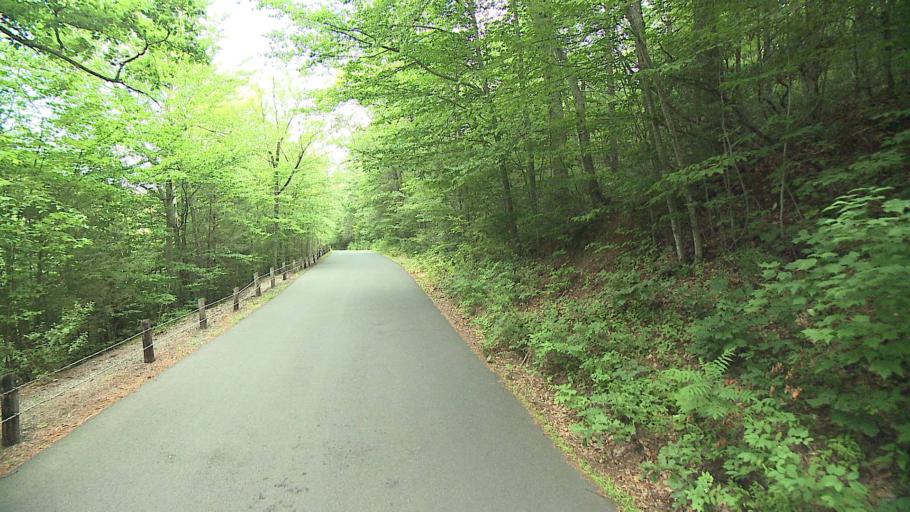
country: US
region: Connecticut
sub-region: Litchfield County
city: New Hartford Center
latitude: 41.9342
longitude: -72.9997
